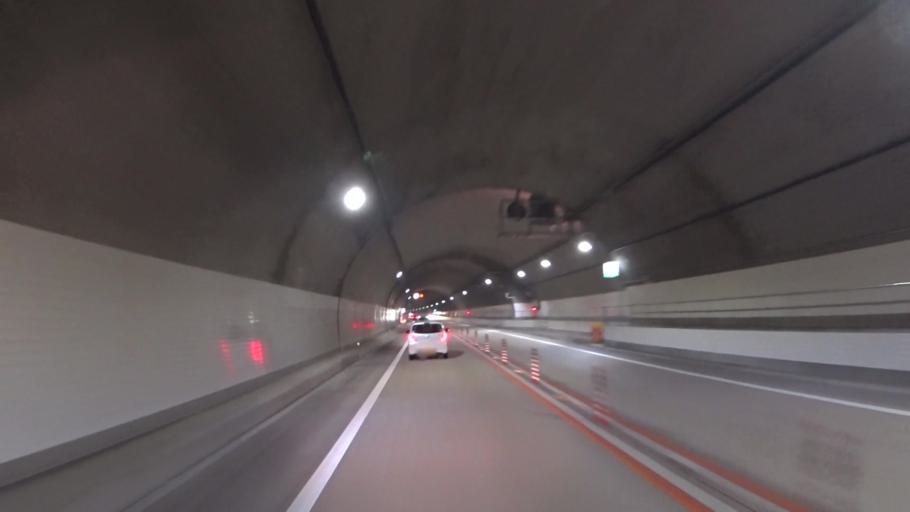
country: JP
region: Kyoto
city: Ayabe
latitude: 35.2384
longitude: 135.3442
